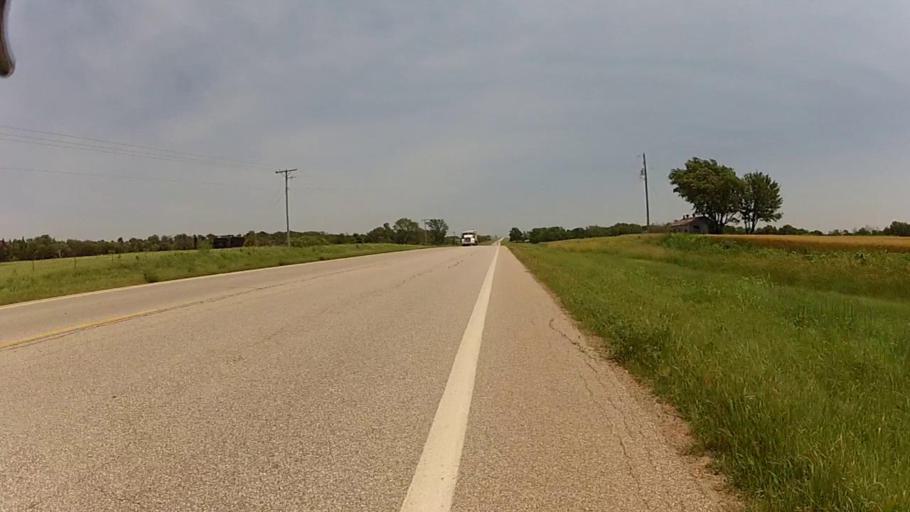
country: US
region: Kansas
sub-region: Cowley County
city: Arkansas City
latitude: 37.0563
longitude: -97.1208
